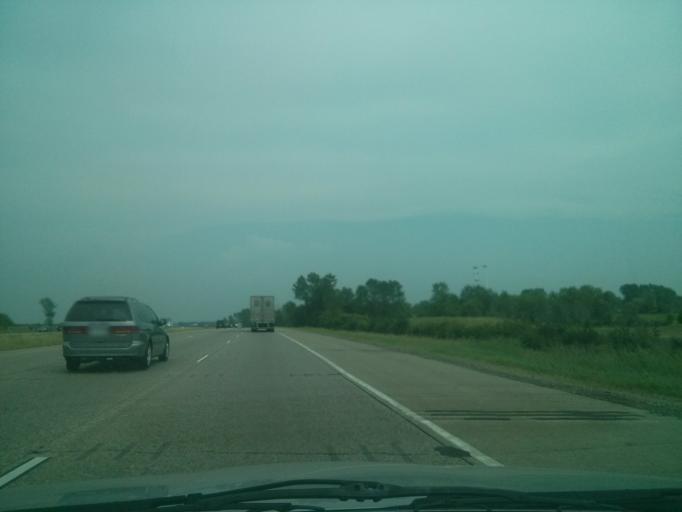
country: US
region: Minnesota
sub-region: Washington County
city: Lakeland
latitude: 44.9497
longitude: -92.8153
